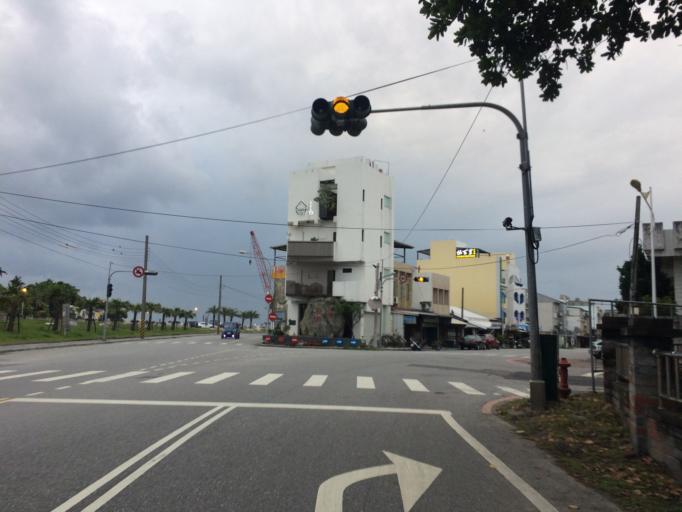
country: TW
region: Taiwan
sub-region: Hualien
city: Hualian
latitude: 23.9772
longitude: 121.6165
